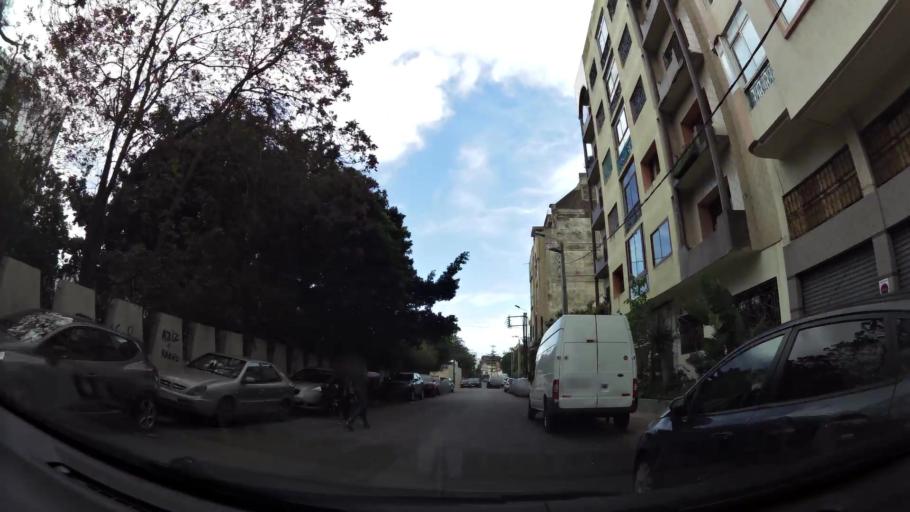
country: MA
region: Grand Casablanca
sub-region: Casablanca
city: Casablanca
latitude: 33.5702
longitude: -7.6229
